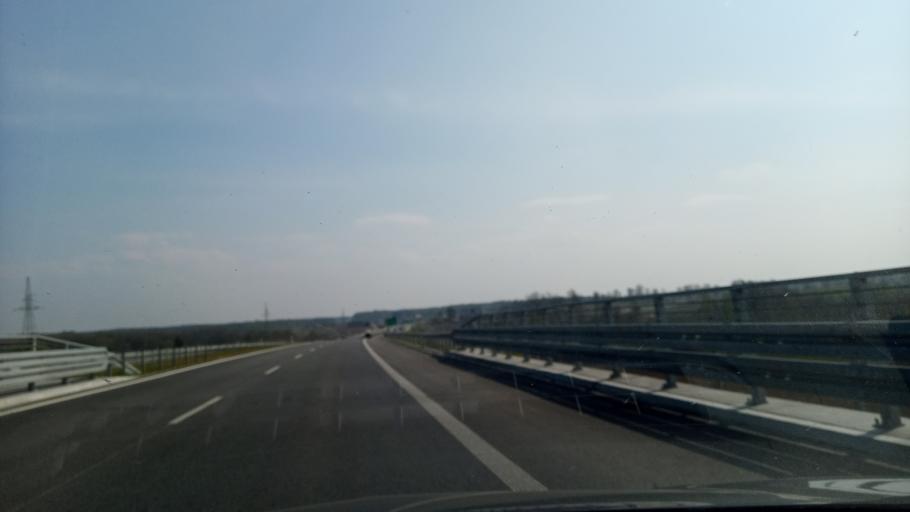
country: PL
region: West Pomeranian Voivodeship
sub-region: Powiat szczecinecki
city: Szczecinek
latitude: 53.7018
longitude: 16.7291
